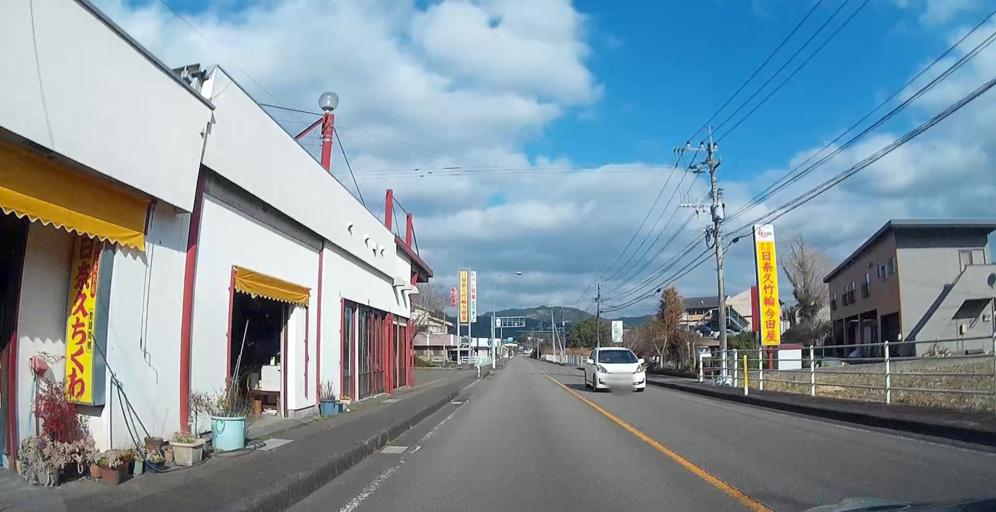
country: JP
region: Kumamoto
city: Yatsushiro
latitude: 32.3977
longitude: 130.5505
